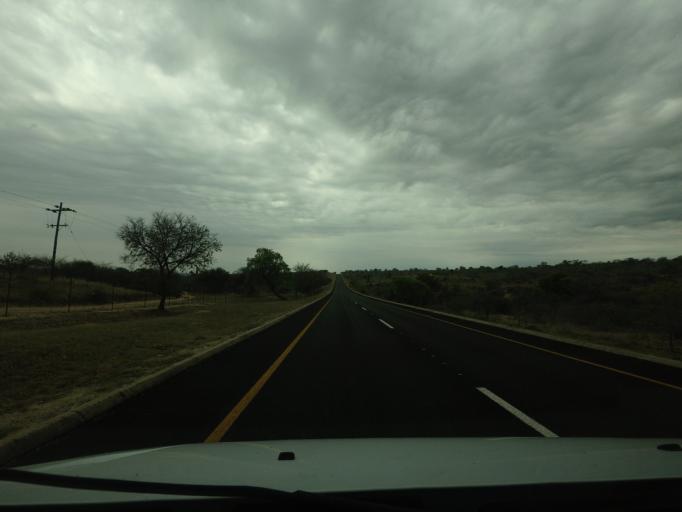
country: ZA
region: Limpopo
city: Thulamahashi
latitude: -24.5650
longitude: 31.1207
